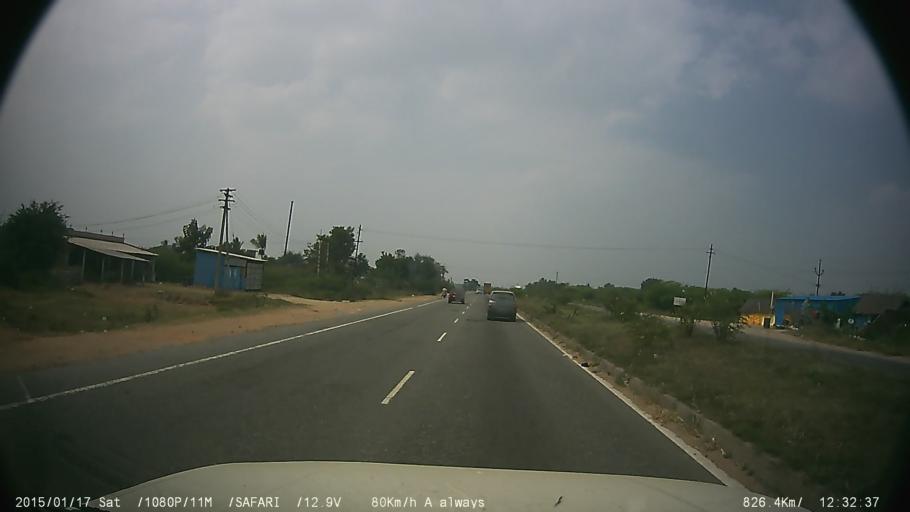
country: IN
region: Tamil Nadu
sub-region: Kancheepuram
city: Kanchipuram
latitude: 12.8700
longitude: 79.6448
